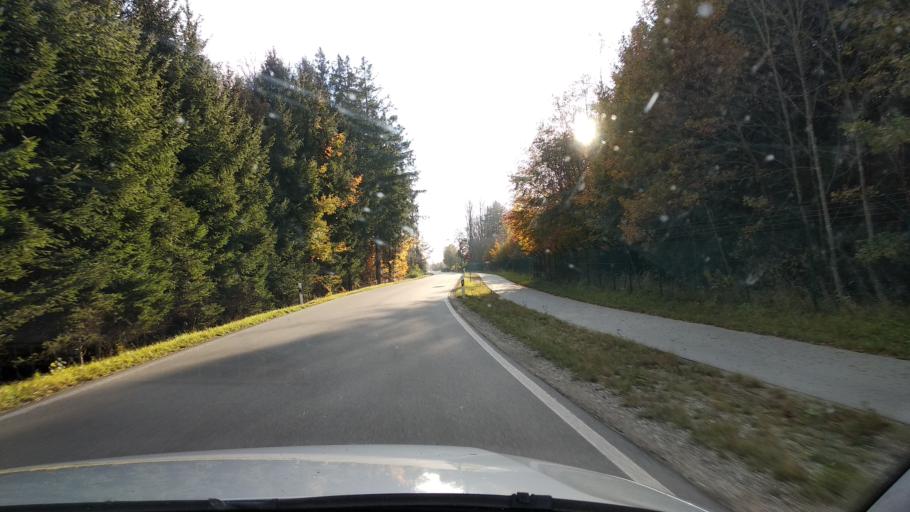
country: DE
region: Bavaria
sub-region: Upper Bavaria
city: Hohenkirchen-Siegertsbrunn
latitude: 48.0334
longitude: 11.7422
